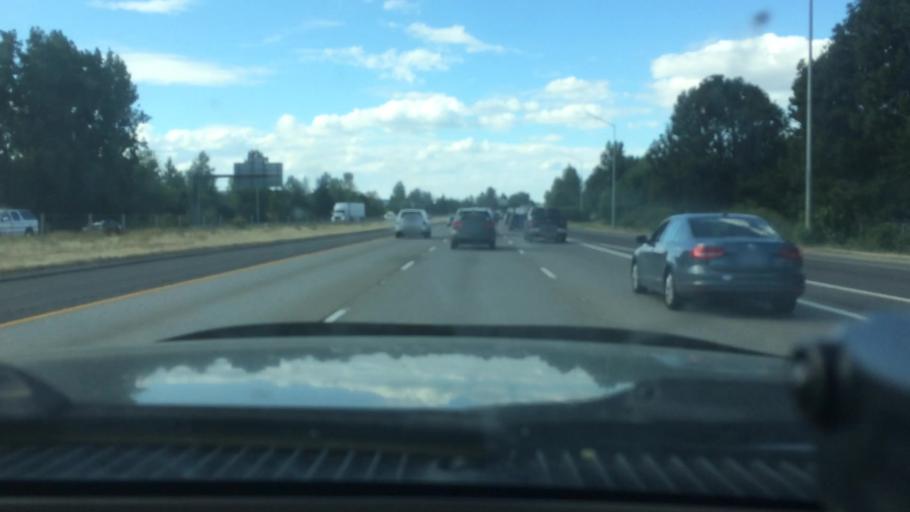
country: US
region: Oregon
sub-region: Marion County
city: Four Corners
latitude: 44.9195
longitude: -122.9896
